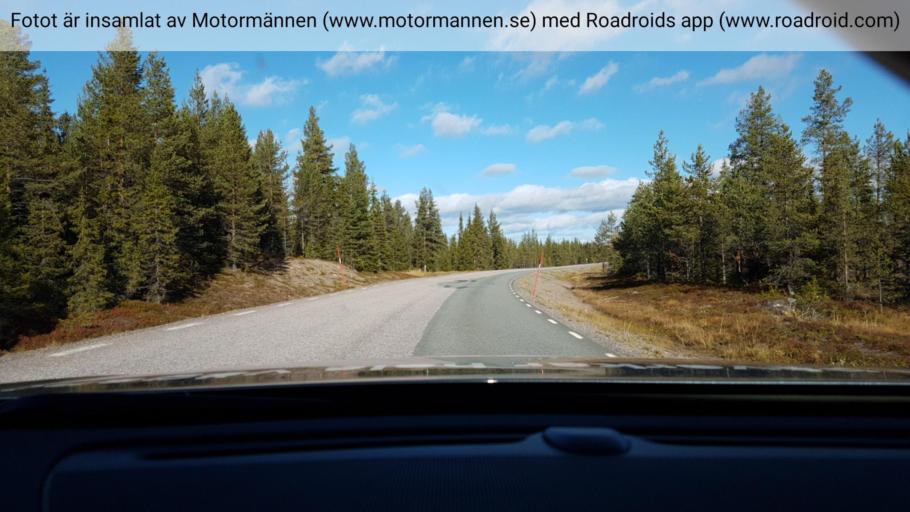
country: SE
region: Norrbotten
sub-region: Arjeplogs Kommun
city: Arjeplog
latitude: 65.8477
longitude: 18.4037
